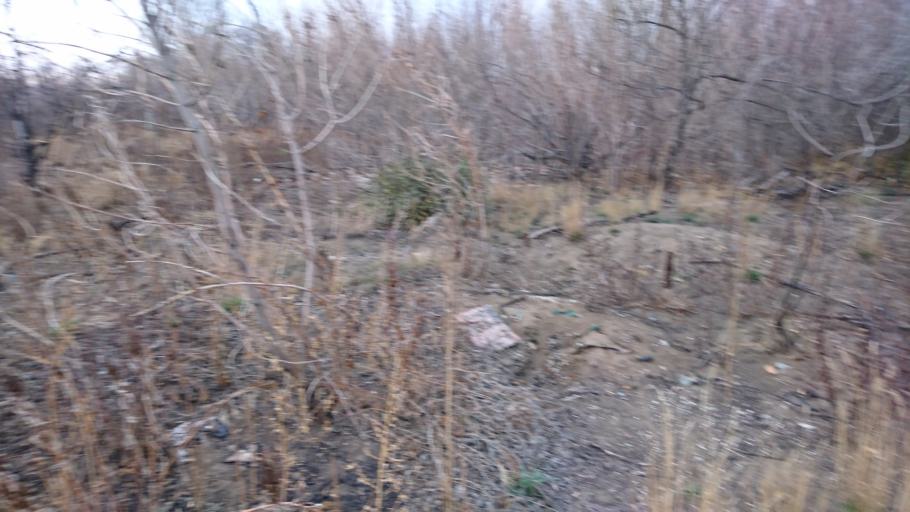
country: RU
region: Orenburg
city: Novotroitsk
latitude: 51.1667
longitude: 58.3125
